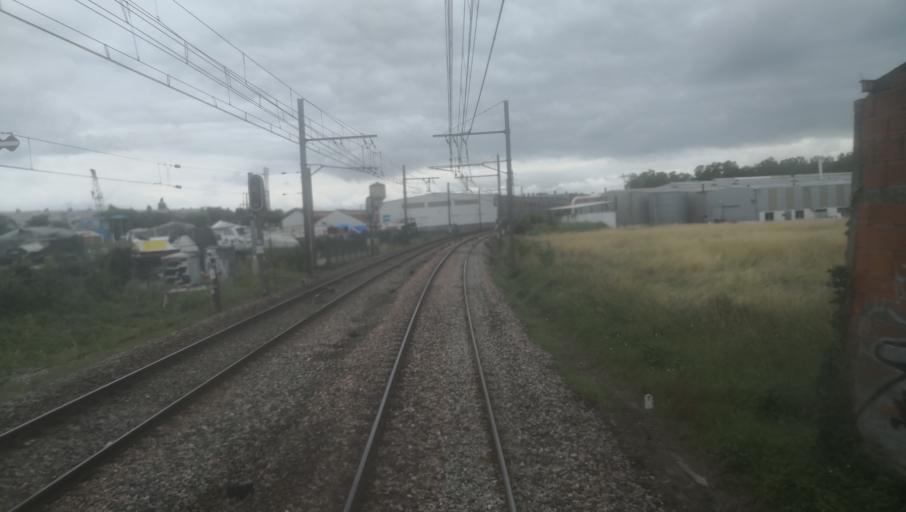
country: FR
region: Midi-Pyrenees
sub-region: Departement du Tarn-et-Garonne
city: Castelsarrasin
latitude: 44.0439
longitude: 1.1110
